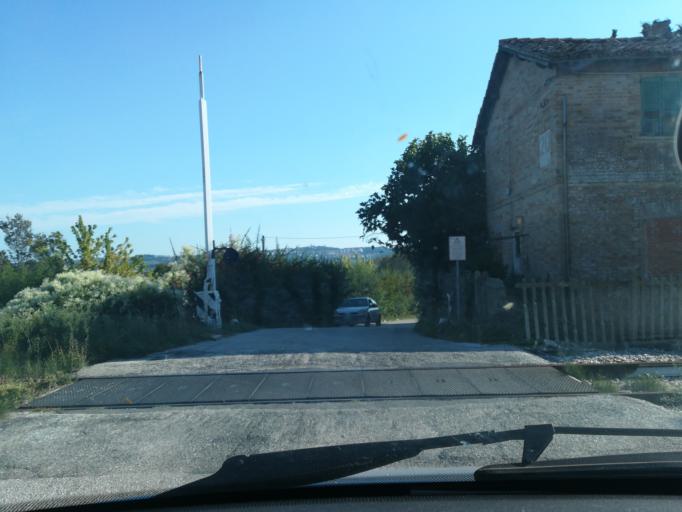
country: IT
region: The Marches
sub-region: Provincia di Macerata
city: Piediripa
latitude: 43.2862
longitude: 13.4881
